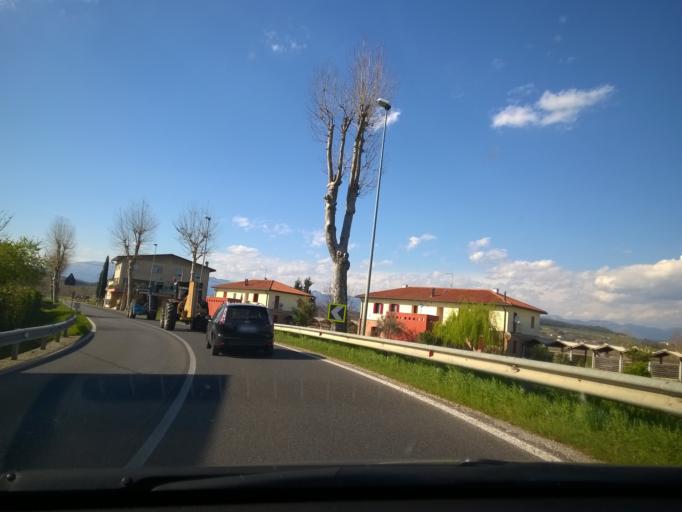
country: IT
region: Veneto
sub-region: Provincia di Treviso
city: Nervesa della Battaglia
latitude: 45.8222
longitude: 12.2223
